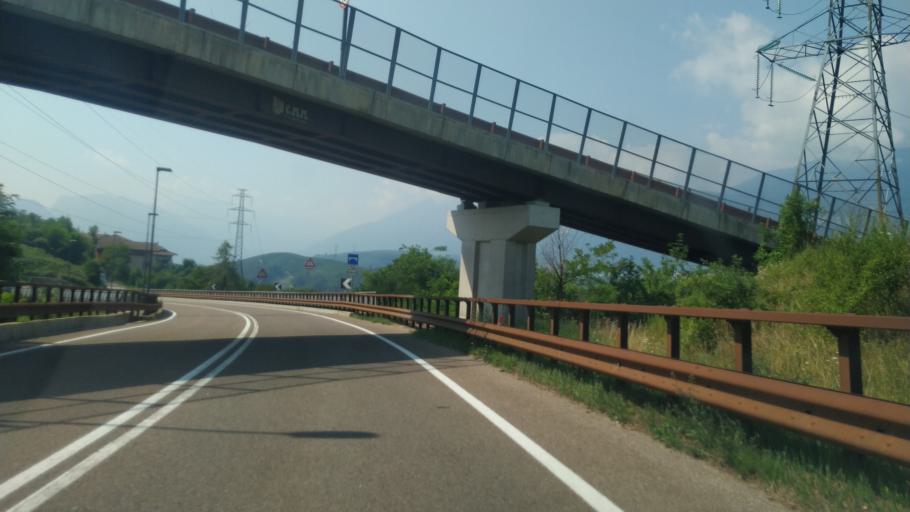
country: IT
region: Trentino-Alto Adige
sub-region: Provincia di Trento
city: Taio
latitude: 46.3241
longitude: 11.0634
